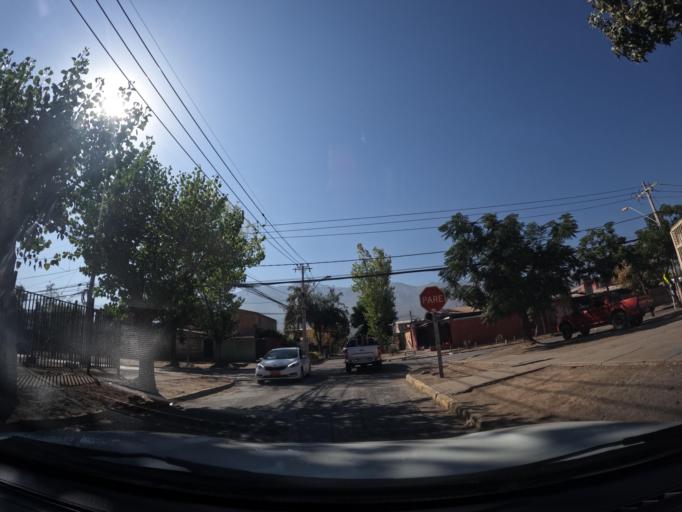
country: CL
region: Santiago Metropolitan
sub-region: Provincia de Santiago
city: Villa Presidente Frei, Nunoa, Santiago, Chile
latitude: -33.4654
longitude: -70.5572
